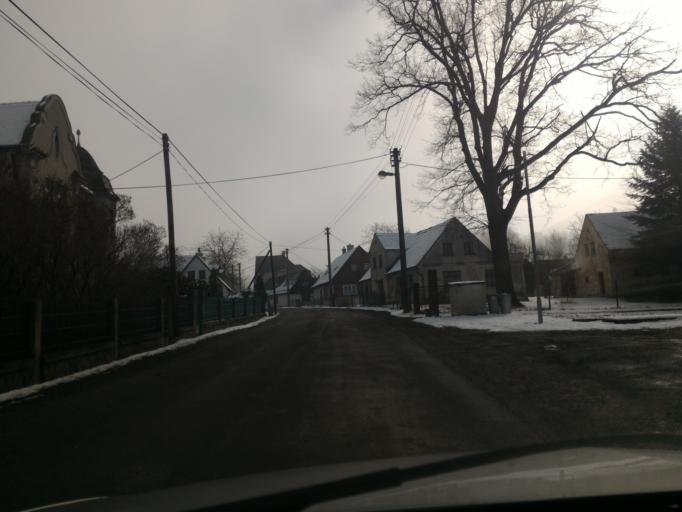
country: CZ
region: Liberecky
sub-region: Okres Liberec
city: Hejnice
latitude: 50.8730
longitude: 15.2247
